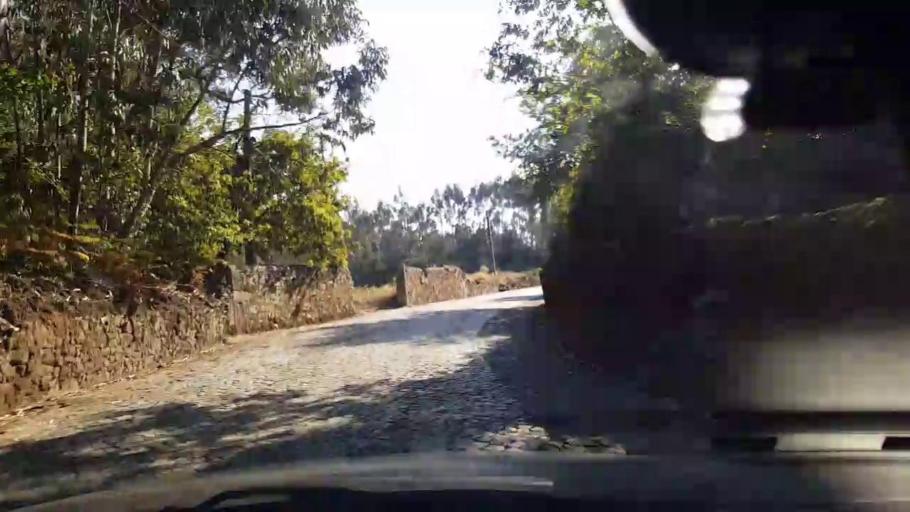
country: PT
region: Porto
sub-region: Vila do Conde
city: Arvore
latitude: 41.3557
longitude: -8.7022
